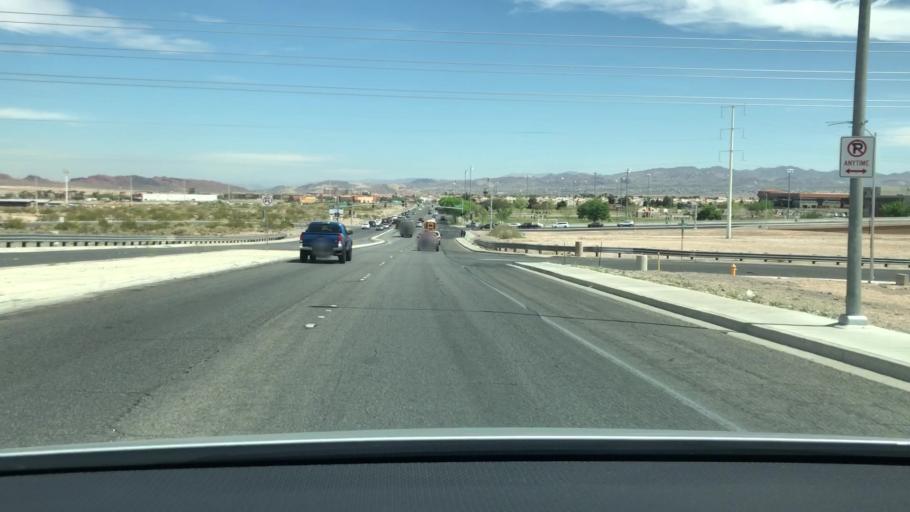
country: US
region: Nevada
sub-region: Clark County
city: Whitney
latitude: 36.0839
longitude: -115.0467
